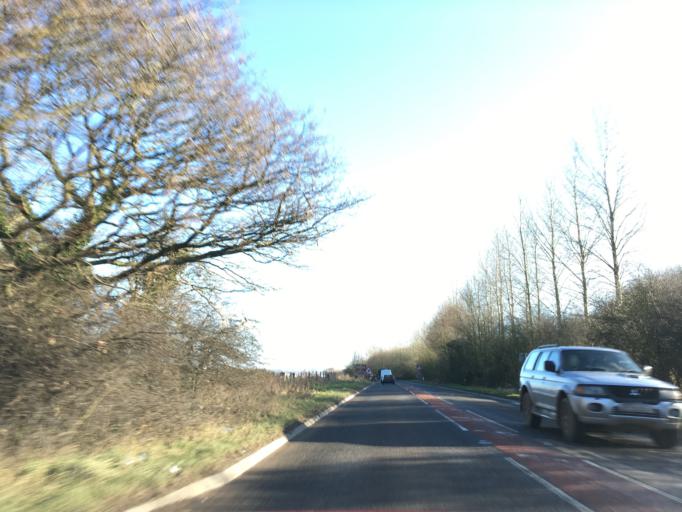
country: GB
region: England
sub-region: Wiltshire
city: Lydiard Tregoze
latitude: 51.5445
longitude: -1.8626
